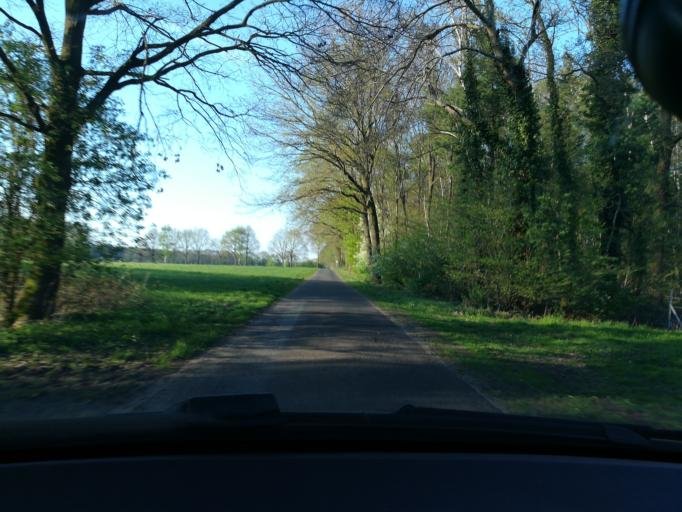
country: DE
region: North Rhine-Westphalia
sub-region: Regierungsbezirk Munster
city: Sassenberg
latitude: 52.0272
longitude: 8.0826
